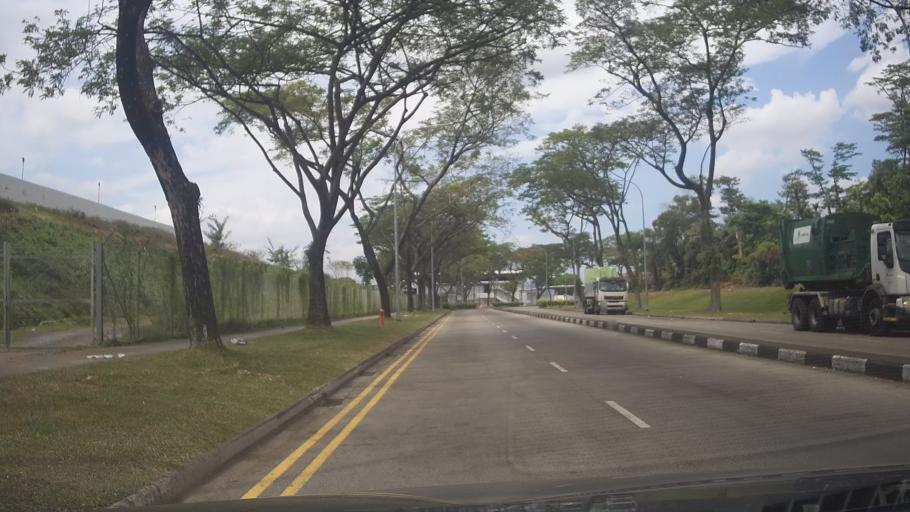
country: MY
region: Johor
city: Johor Bahru
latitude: 1.4590
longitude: 103.7939
